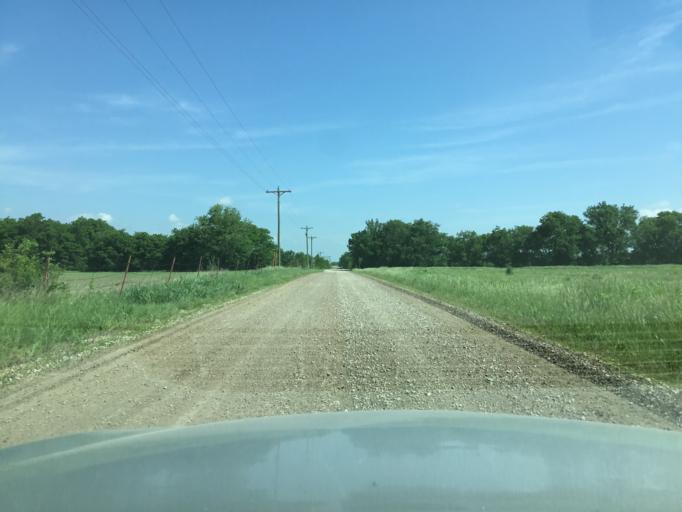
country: US
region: Kansas
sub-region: Labette County
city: Oswego
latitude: 37.1695
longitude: -95.1399
